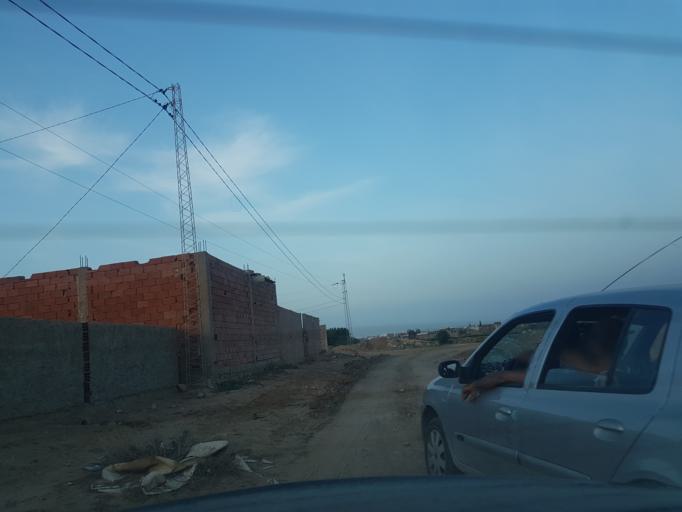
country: TN
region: Safaqis
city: Sfax
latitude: 34.7037
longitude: 10.6957
